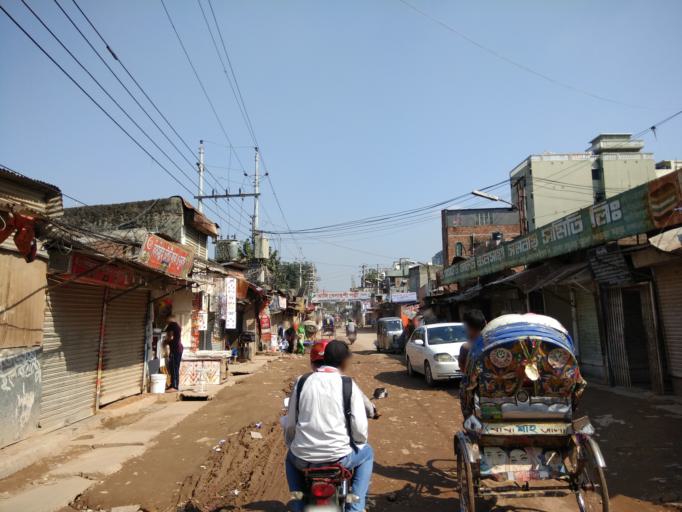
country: BD
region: Dhaka
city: Tungi
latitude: 23.8171
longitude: 90.3699
